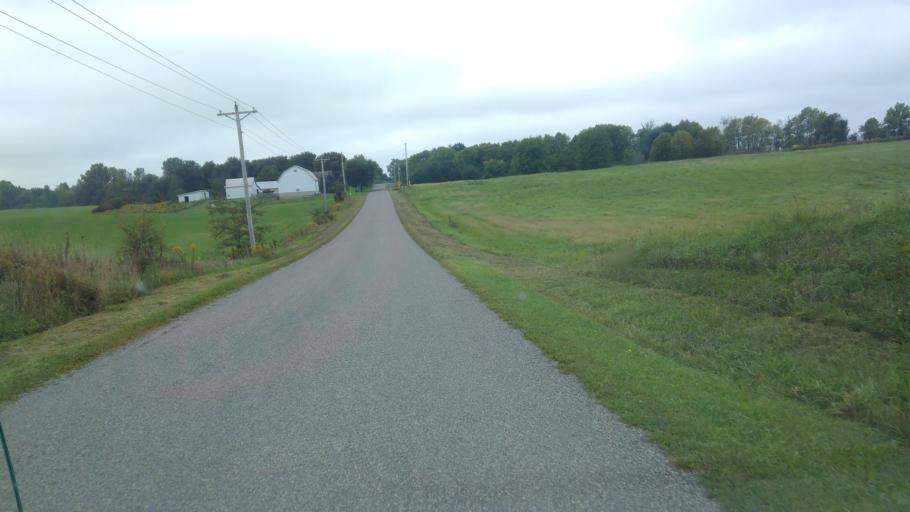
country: US
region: Ohio
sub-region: Hardin County
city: Kenton
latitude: 40.5769
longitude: -83.6753
